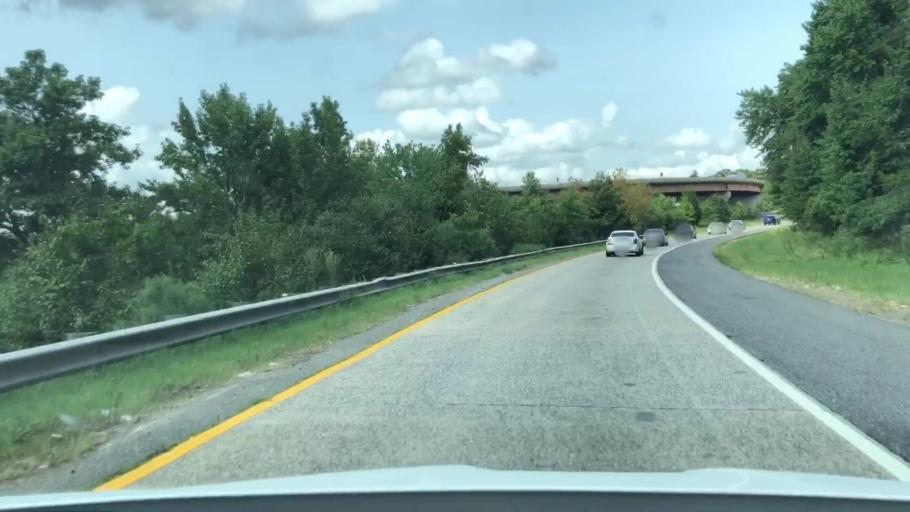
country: US
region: Maryland
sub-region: Prince George's County
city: Glenarden
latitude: 38.9433
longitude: -76.8567
